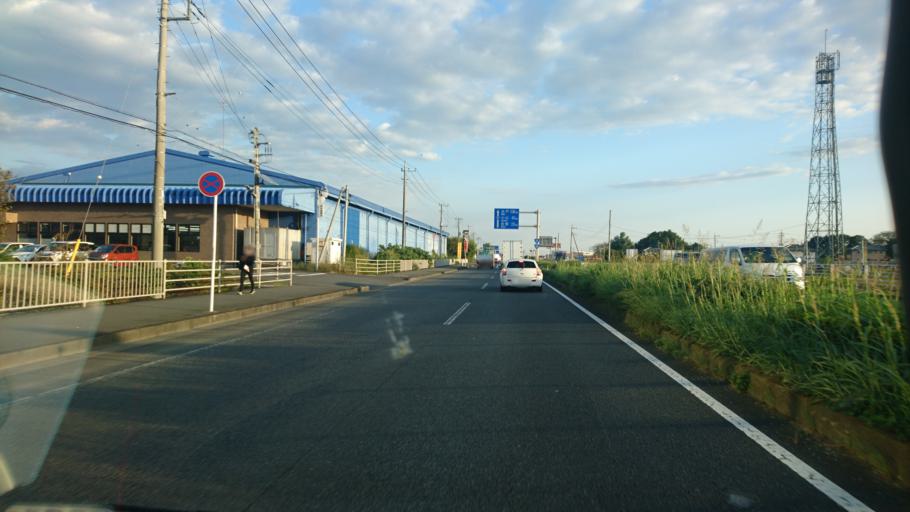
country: JP
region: Gunma
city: Ota
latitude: 36.3461
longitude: 139.3817
